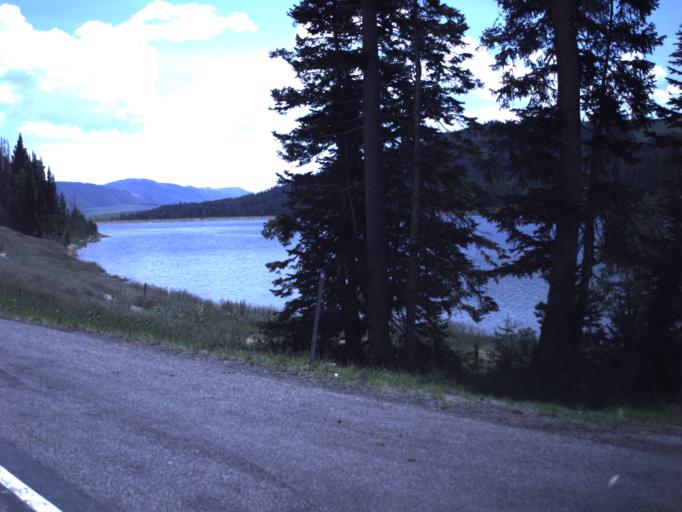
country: US
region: Utah
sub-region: Sanpete County
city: Fairview
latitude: 39.5921
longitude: -111.2651
